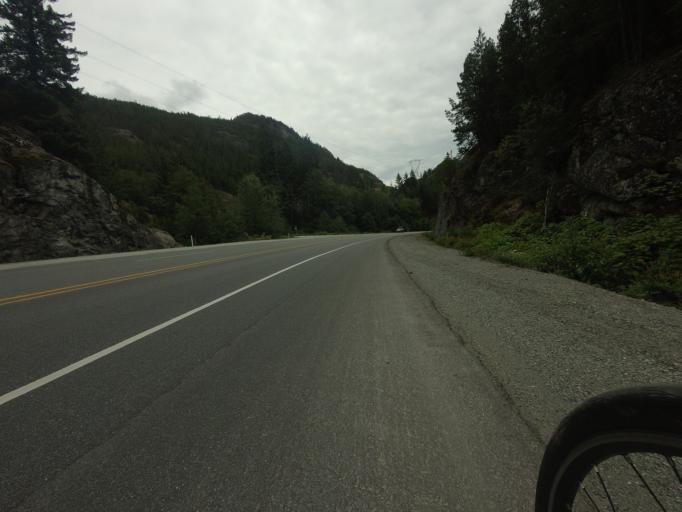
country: CA
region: British Columbia
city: Whistler
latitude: 49.9069
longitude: -123.1630
